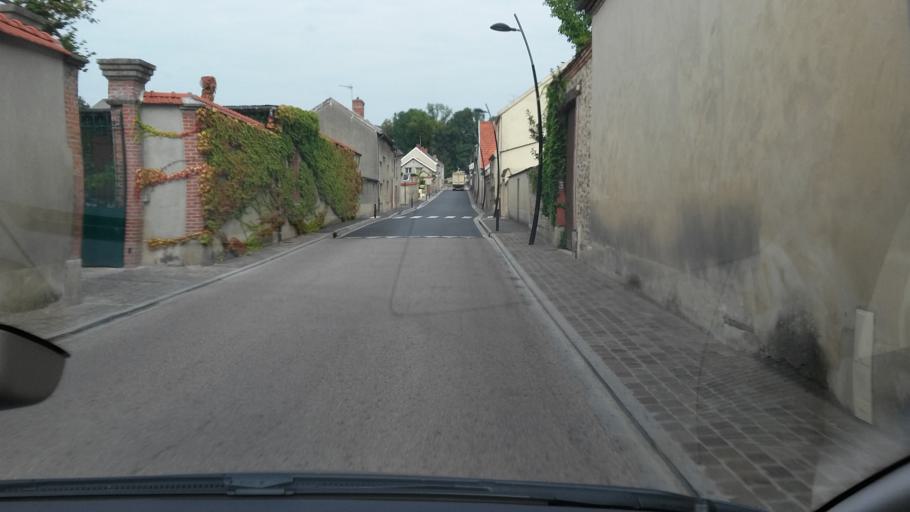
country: FR
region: Champagne-Ardenne
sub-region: Departement de la Marne
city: Tours-sur-Marne
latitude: 49.1016
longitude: 4.1146
